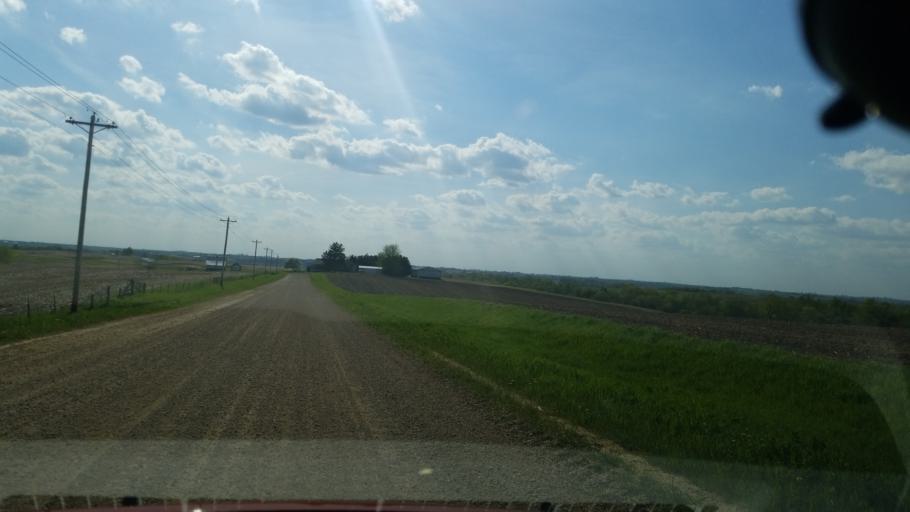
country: US
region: Iowa
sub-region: Jackson County
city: Maquoketa
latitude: 42.2150
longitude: -90.7243
